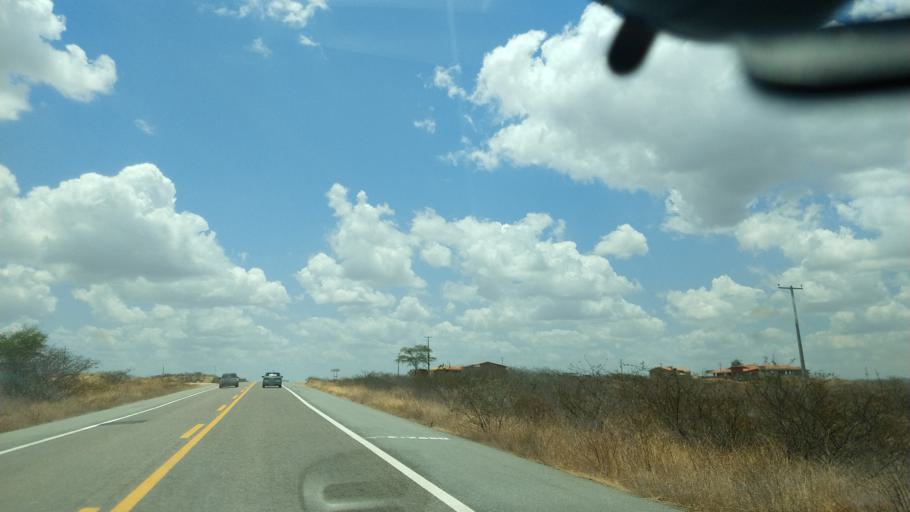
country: BR
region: Rio Grande do Norte
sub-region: Cerro Cora
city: Cerro Cora
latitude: -6.2068
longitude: -36.3183
